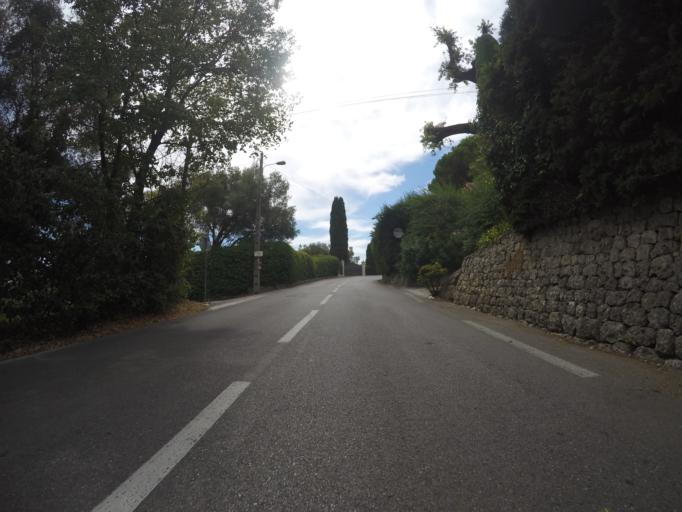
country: FR
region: Provence-Alpes-Cote d'Azur
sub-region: Departement des Alpes-Maritimes
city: Mougins
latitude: 43.6017
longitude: 6.9979
